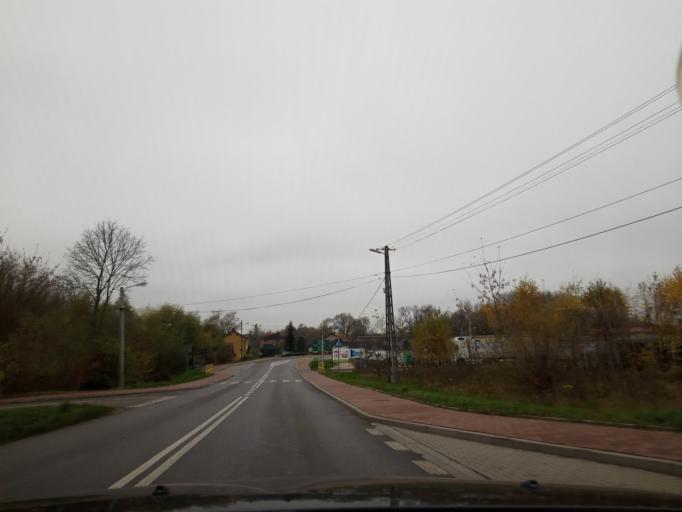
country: PL
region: Swietokrzyskie
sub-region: Powiat pinczowski
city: Dzialoszyce
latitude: 50.3582
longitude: 20.3530
